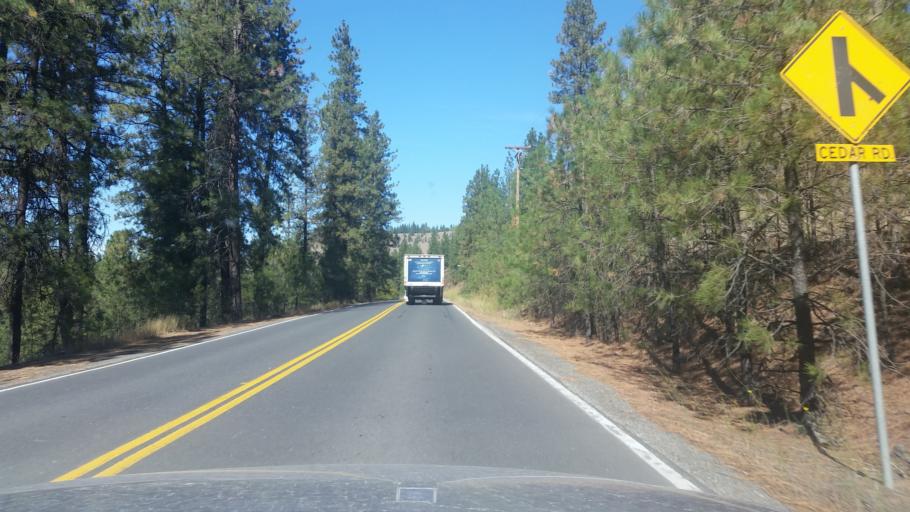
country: US
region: Washington
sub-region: Spokane County
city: Spokane
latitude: 47.6059
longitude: -117.4336
